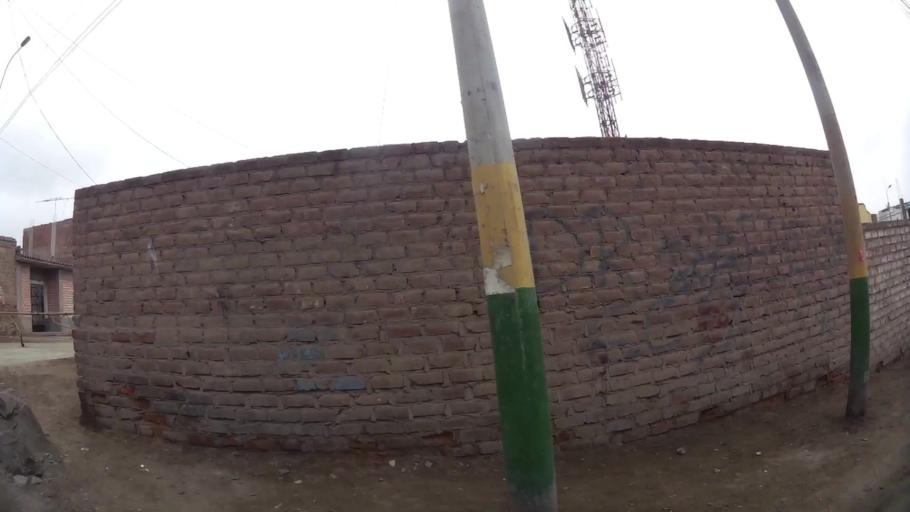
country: PE
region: Lima
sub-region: Lima
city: Cieneguilla
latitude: -12.2192
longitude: -76.9060
